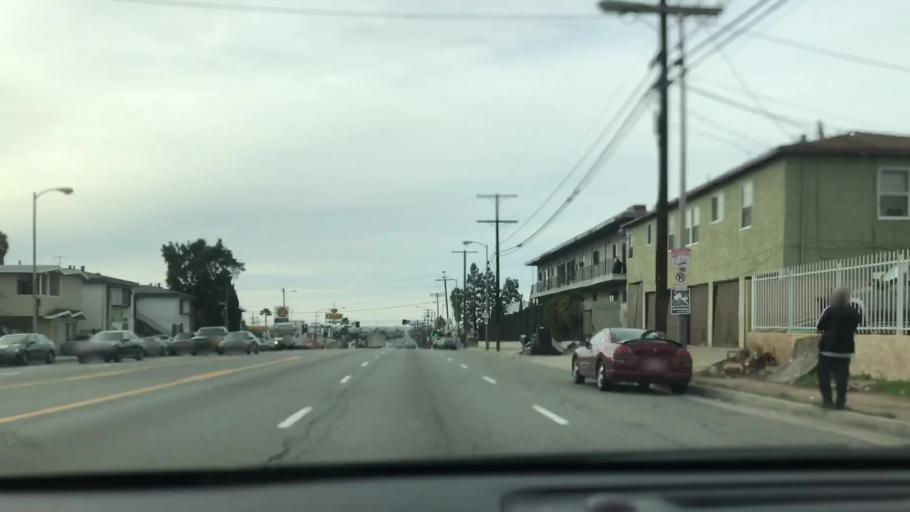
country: US
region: California
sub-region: Los Angeles County
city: West Athens
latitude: 33.9165
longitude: -118.2895
